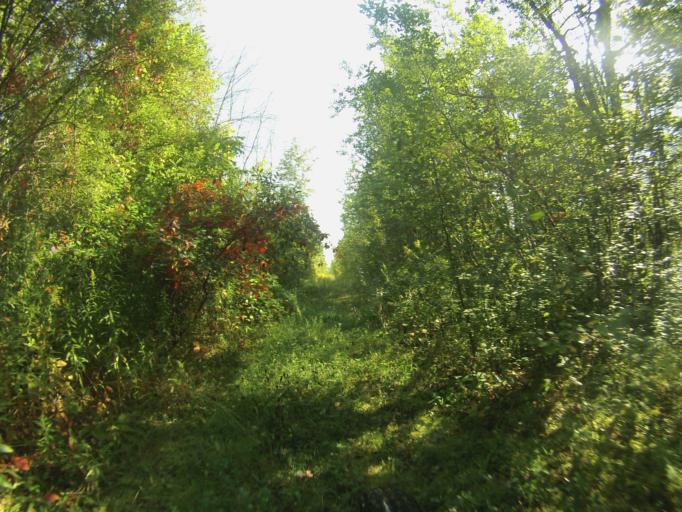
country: CA
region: Ontario
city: Ottawa
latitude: 45.3736
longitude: -75.6344
